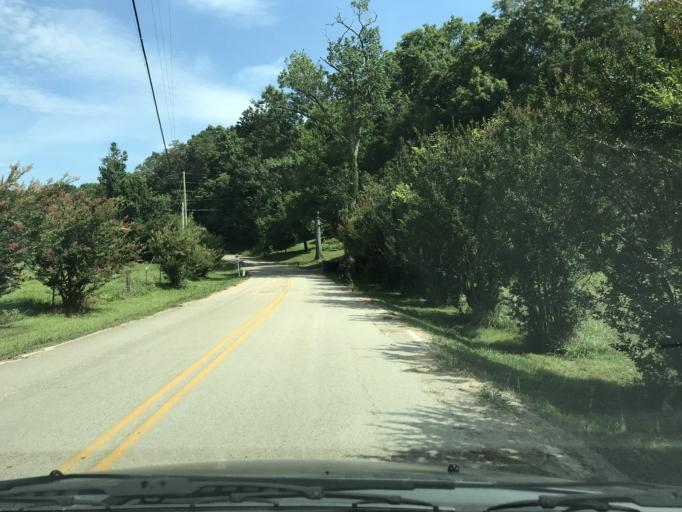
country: US
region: Tennessee
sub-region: Hamilton County
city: Lakesite
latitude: 35.2252
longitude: -85.0164
